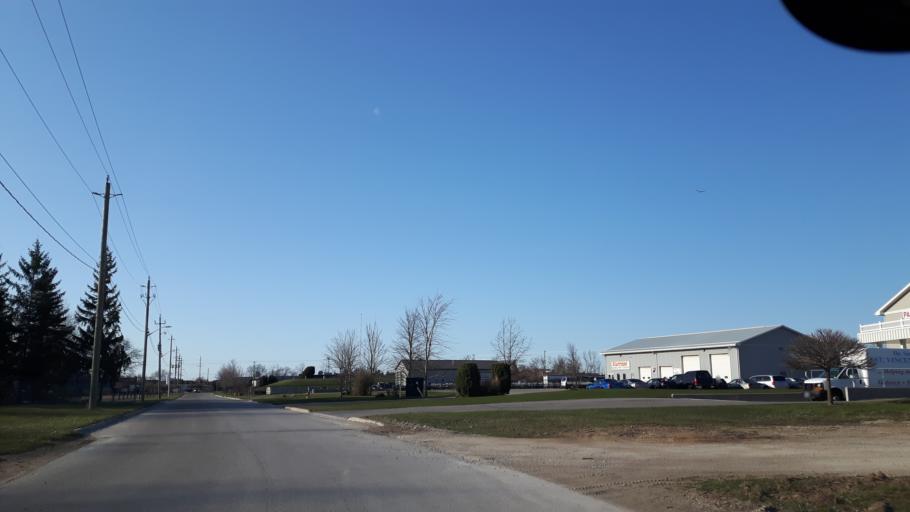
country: CA
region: Ontario
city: Goderich
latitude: 43.7286
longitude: -81.6937
